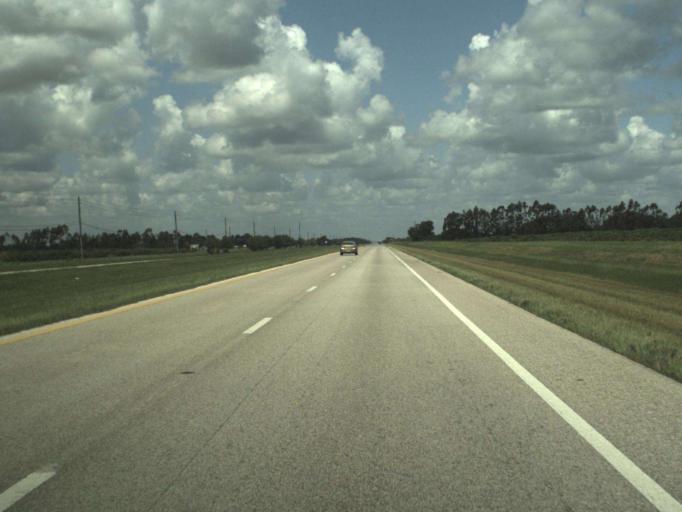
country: US
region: Florida
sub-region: Indian River County
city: Fellsmere
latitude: 27.6403
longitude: -80.6221
